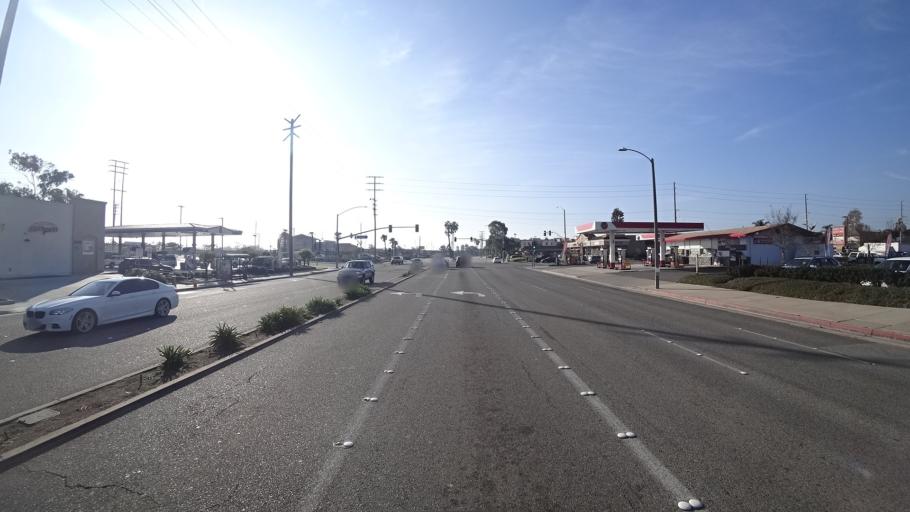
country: US
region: California
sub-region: Orange County
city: Costa Mesa
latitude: 33.6513
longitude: -117.9536
